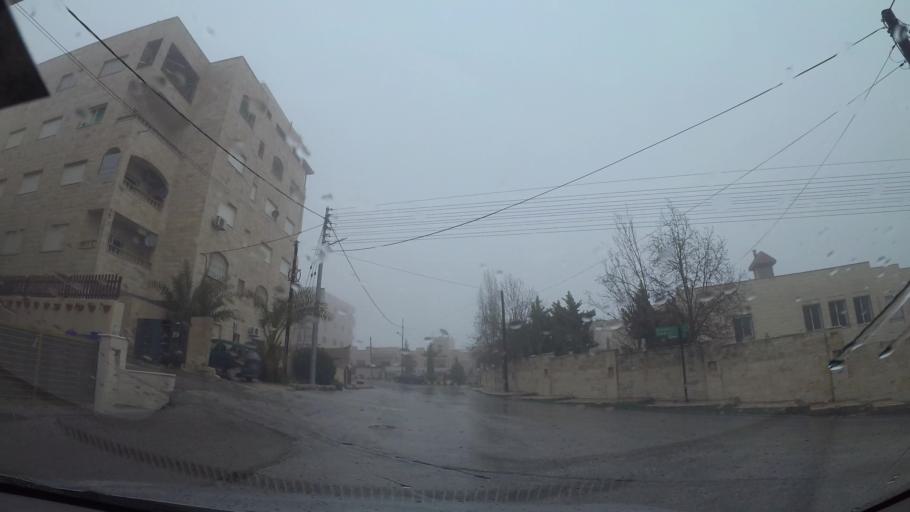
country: JO
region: Amman
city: Al Jubayhah
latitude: 32.0149
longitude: 35.8884
